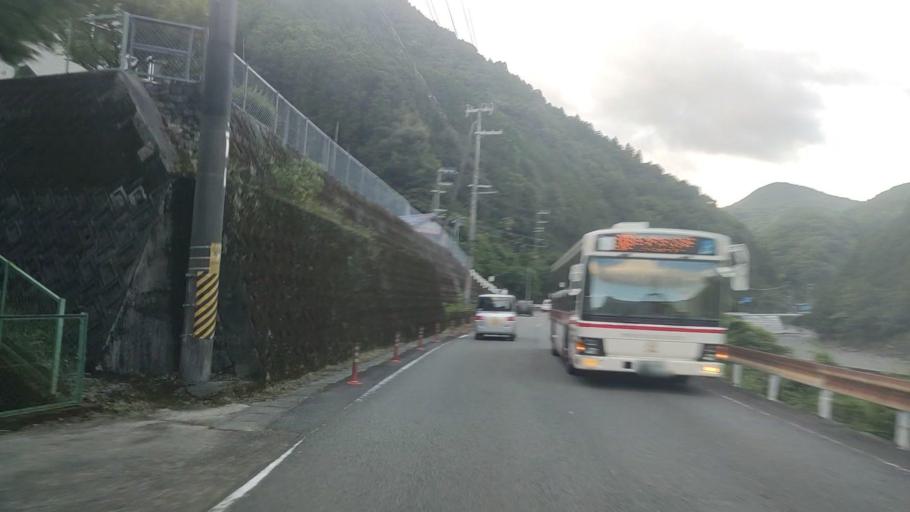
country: JP
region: Wakayama
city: Tanabe
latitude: 33.7847
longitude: 135.5052
